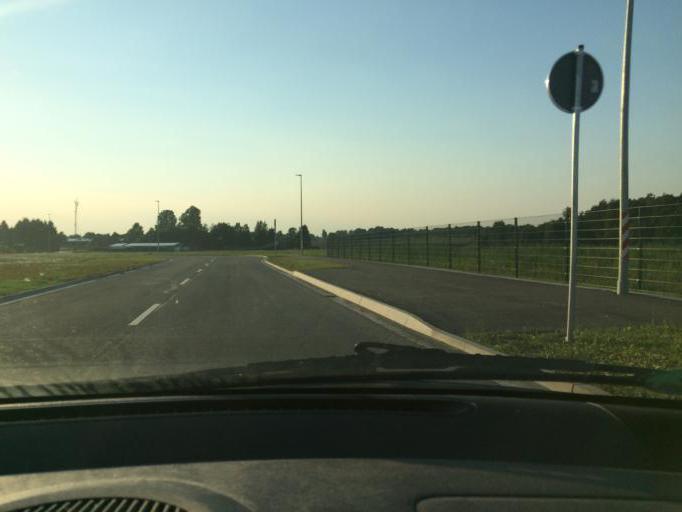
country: DE
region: Lower Saxony
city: Walsrode
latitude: 52.8481
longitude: 9.5583
